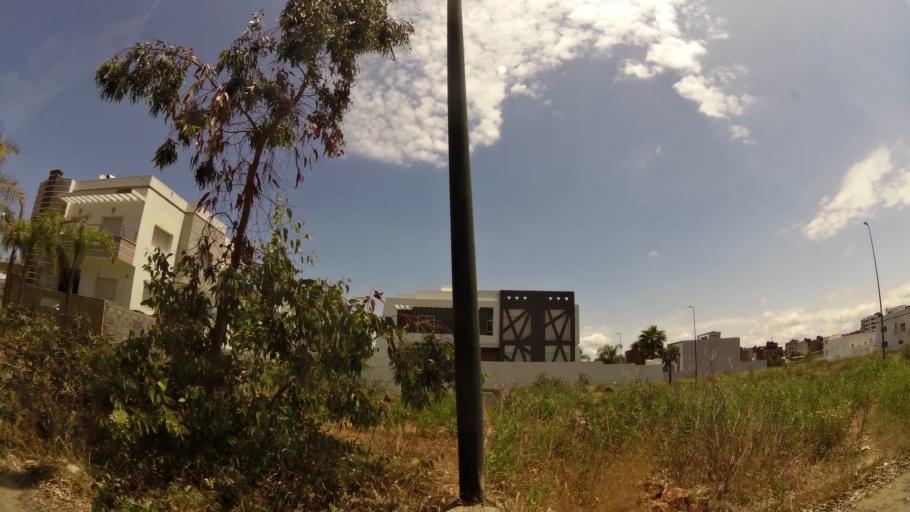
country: MA
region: Gharb-Chrarda-Beni Hssen
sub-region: Kenitra Province
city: Kenitra
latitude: 34.2637
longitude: -6.6305
